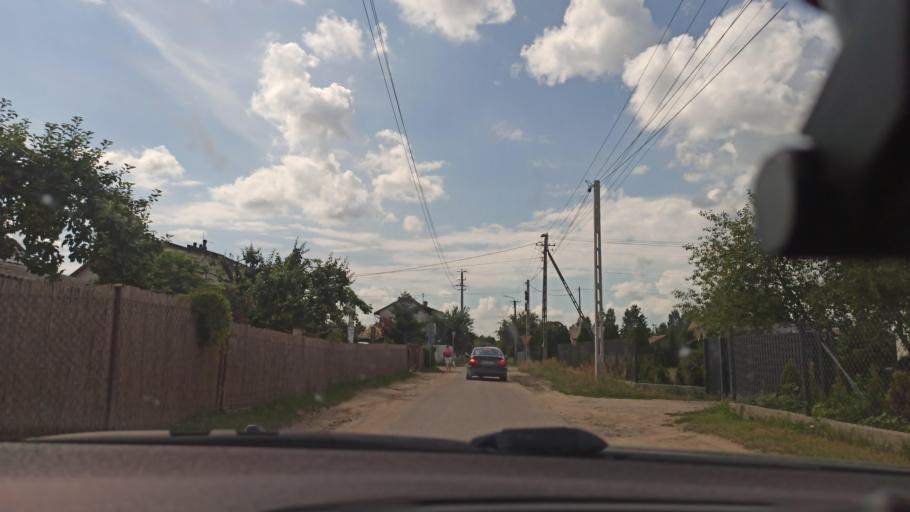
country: PL
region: Podlasie
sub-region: Powiat bialostocki
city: Turosn Koscielna
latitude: 53.0687
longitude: 23.1020
